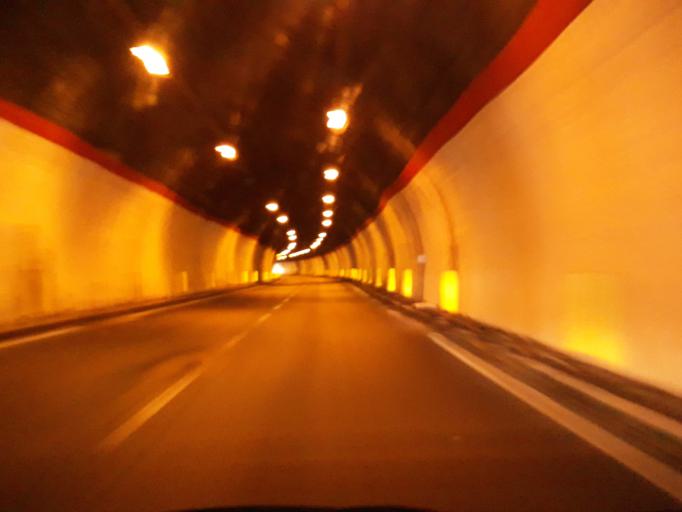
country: IT
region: Sicily
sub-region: Palermo
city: Termini Imerese
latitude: 37.9749
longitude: 13.6825
